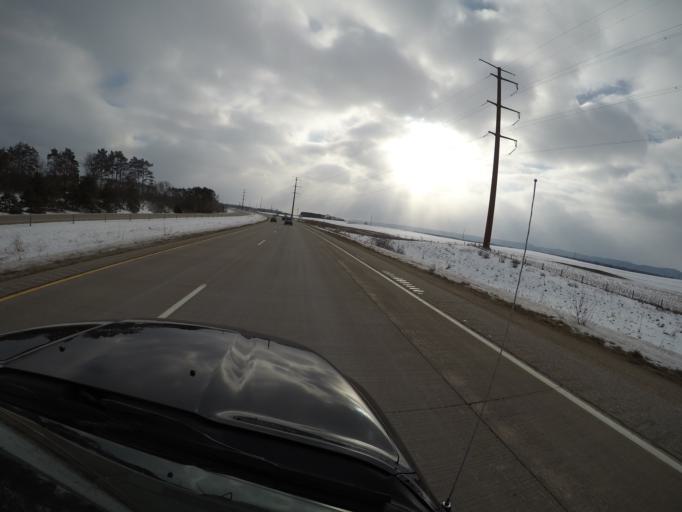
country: US
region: Wisconsin
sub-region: La Crosse County
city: Brice Prairie
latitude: 43.9636
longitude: -91.2863
